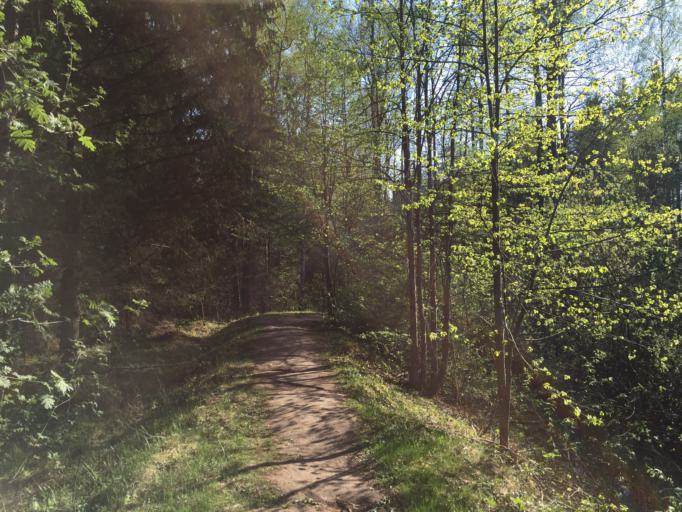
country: LV
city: Tireli
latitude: 56.8303
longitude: 23.7054
